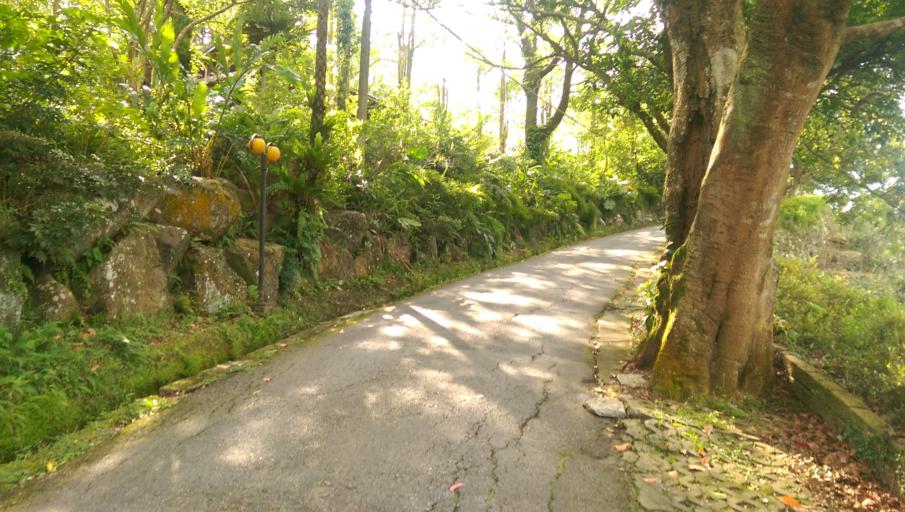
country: TW
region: Taipei
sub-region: Taipei
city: Banqiao
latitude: 24.9327
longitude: 121.5417
